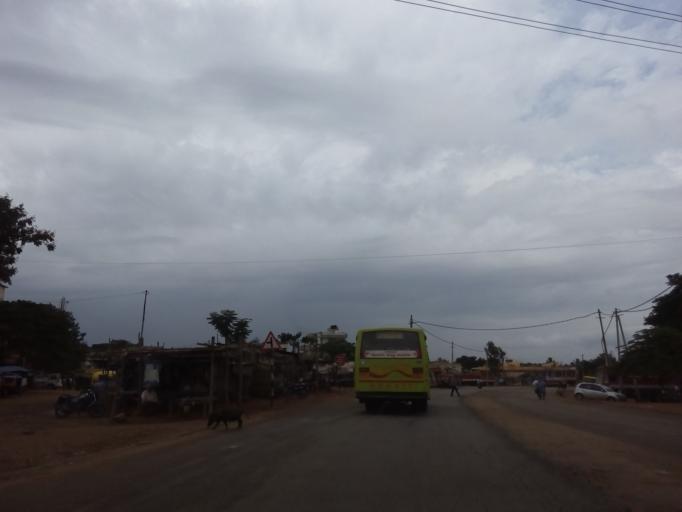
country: IN
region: Karnataka
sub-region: Davanagere
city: Harihar
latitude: 14.5208
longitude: 75.7871
